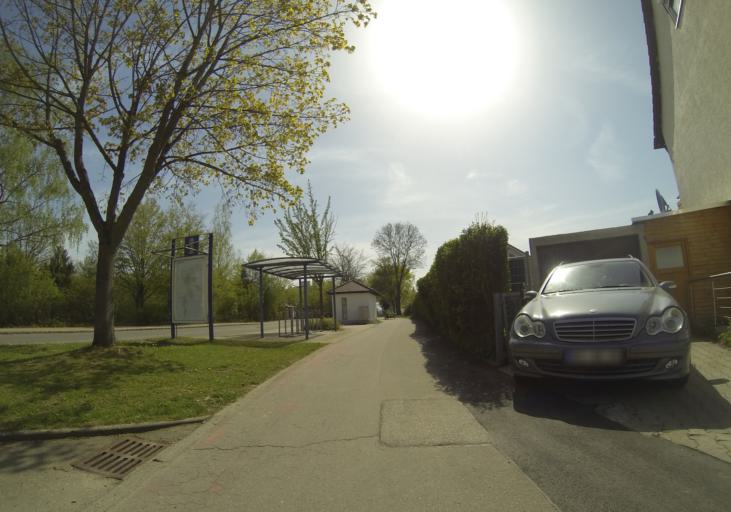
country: DE
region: Baden-Wuerttemberg
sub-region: Tuebingen Region
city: Laupheim
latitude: 48.2354
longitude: 9.8885
